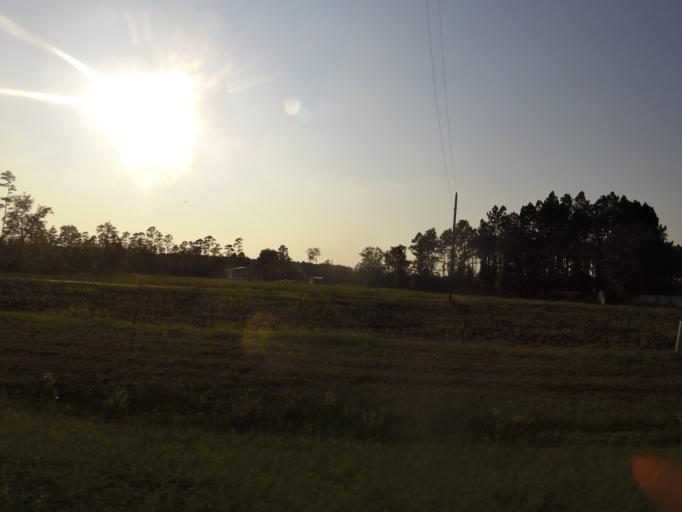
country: US
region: Florida
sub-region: Nassau County
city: Callahan
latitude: 30.5362
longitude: -81.9881
